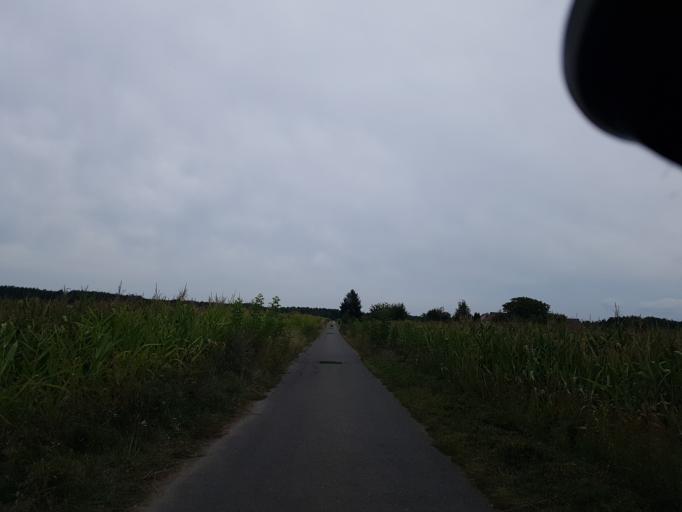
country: DE
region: Brandenburg
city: Finsterwalde
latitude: 51.6096
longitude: 13.6619
